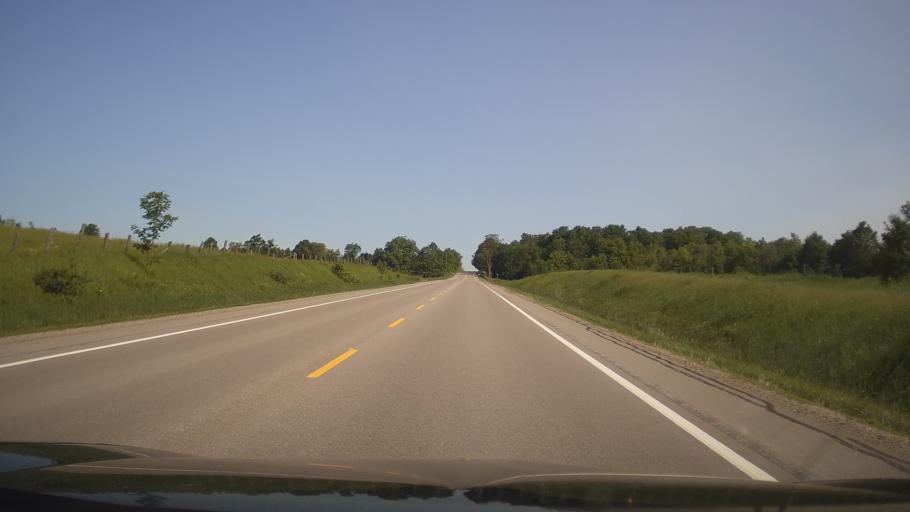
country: CA
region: Ontario
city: Omemee
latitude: 44.3952
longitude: -78.9073
